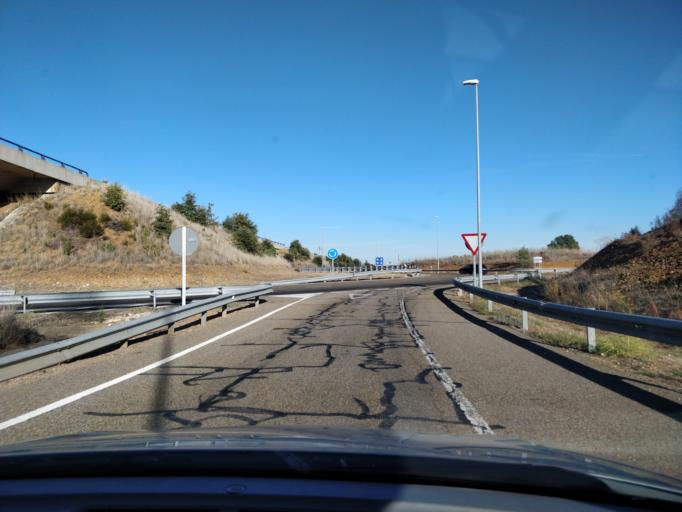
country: ES
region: Castille and Leon
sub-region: Provincia de Leon
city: San Andres del Rabanedo
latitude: 42.5762
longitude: -5.6214
